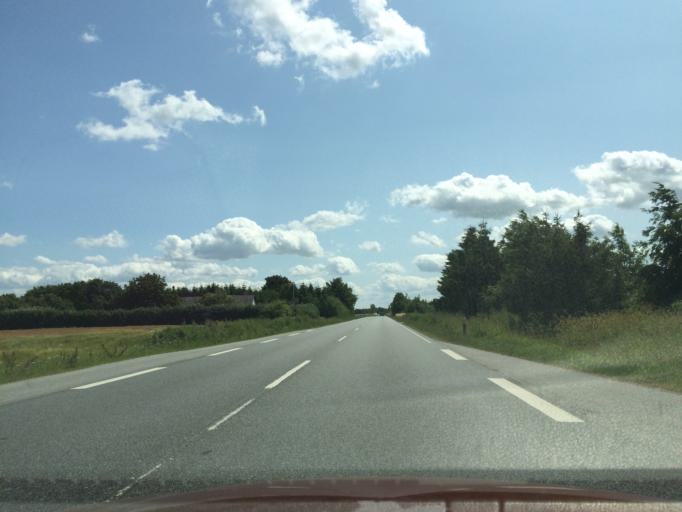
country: DK
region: Central Jutland
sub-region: Favrskov Kommune
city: Hammel
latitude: 56.2574
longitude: 9.7558
